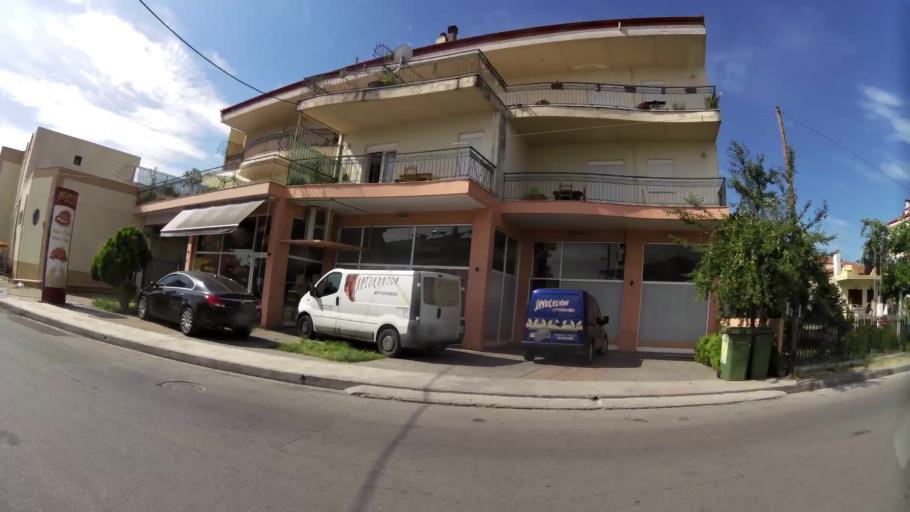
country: GR
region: Central Macedonia
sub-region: Nomos Pierias
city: Katerini
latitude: 40.2803
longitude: 22.4963
